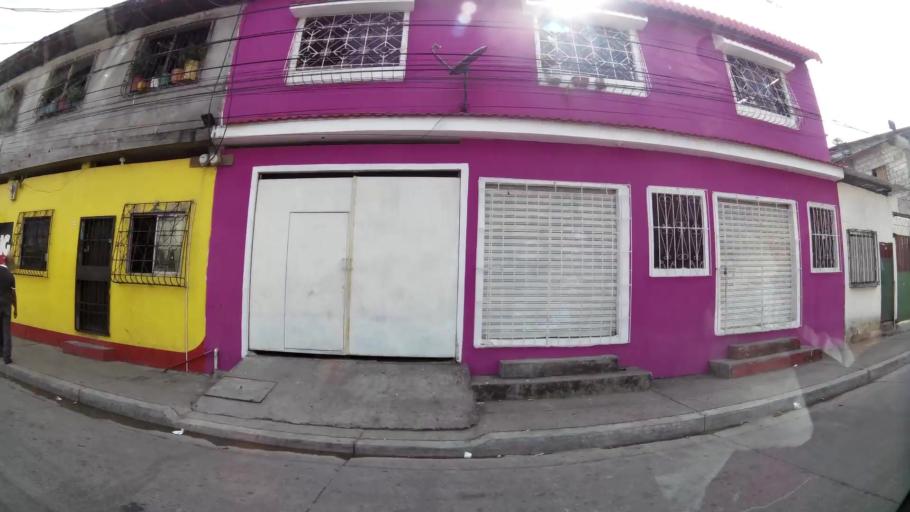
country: EC
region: Guayas
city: Guayaquil
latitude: -2.2539
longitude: -79.8767
